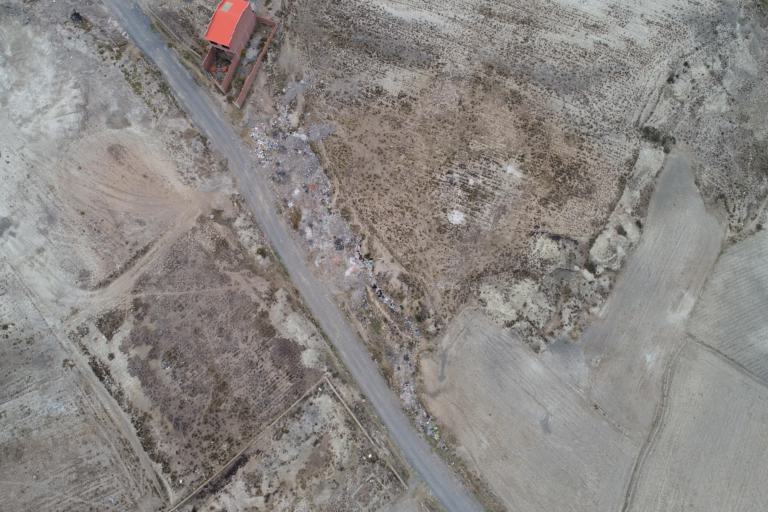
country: BO
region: La Paz
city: Achacachi
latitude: -16.0430
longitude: -68.6944
